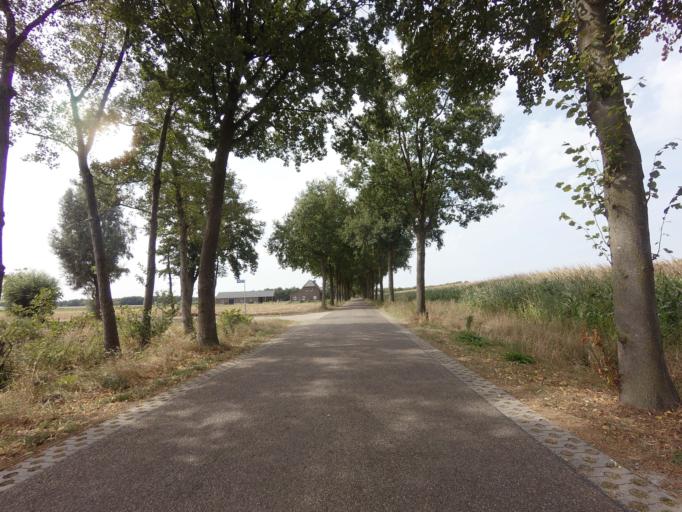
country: NL
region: North Brabant
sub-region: Gemeente Helmond
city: Helmond
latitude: 51.4922
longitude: 5.7233
